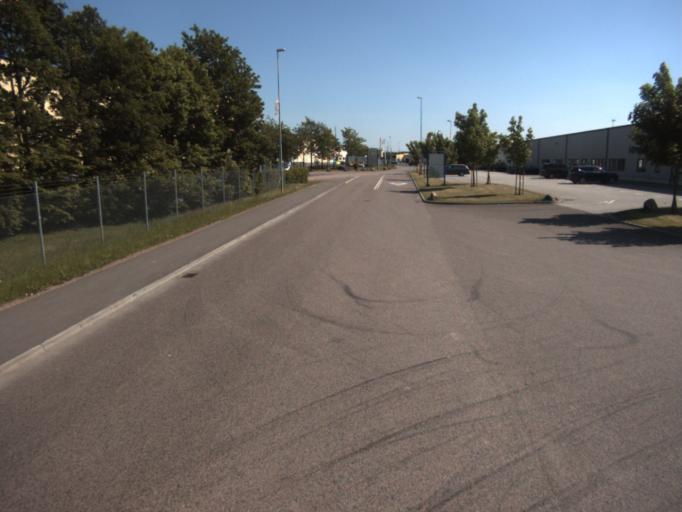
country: SE
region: Skane
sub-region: Helsingborg
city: Barslov
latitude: 56.0462
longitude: 12.7793
